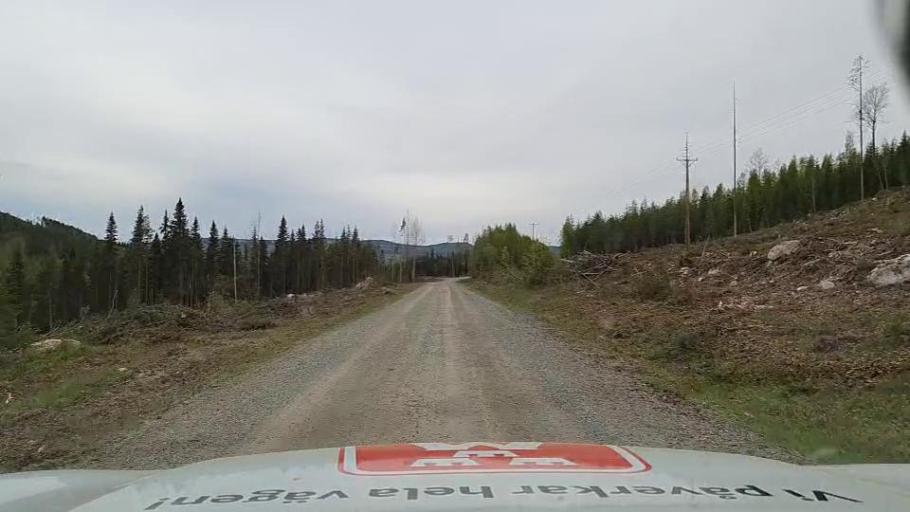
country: SE
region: Jaemtland
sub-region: Bergs Kommun
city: Hoverberg
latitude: 62.5265
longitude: 14.7114
